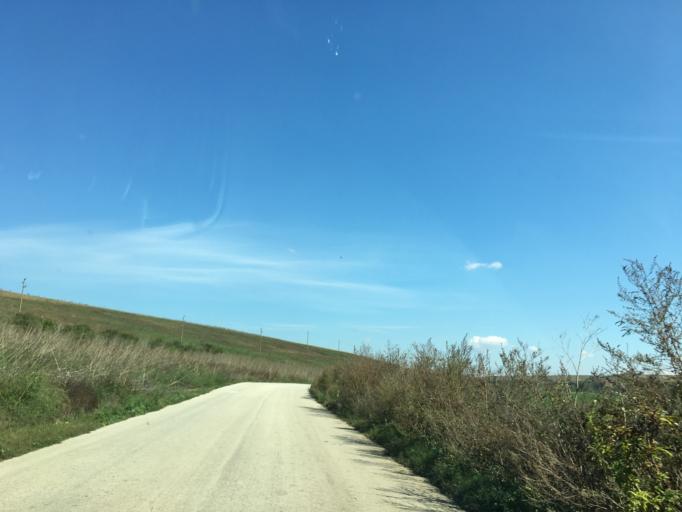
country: BG
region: Pleven
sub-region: Obshtina Knezha
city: Knezha
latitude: 43.5531
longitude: 24.1816
